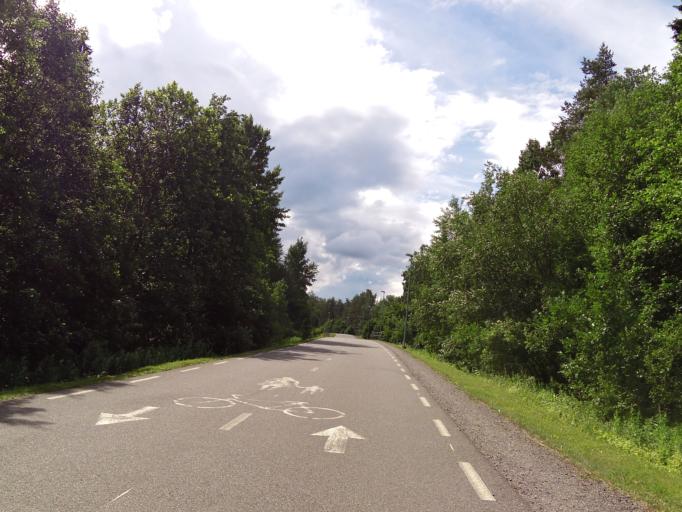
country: EE
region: Harju
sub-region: Saue vald
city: Laagri
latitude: 59.3912
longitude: 24.6257
